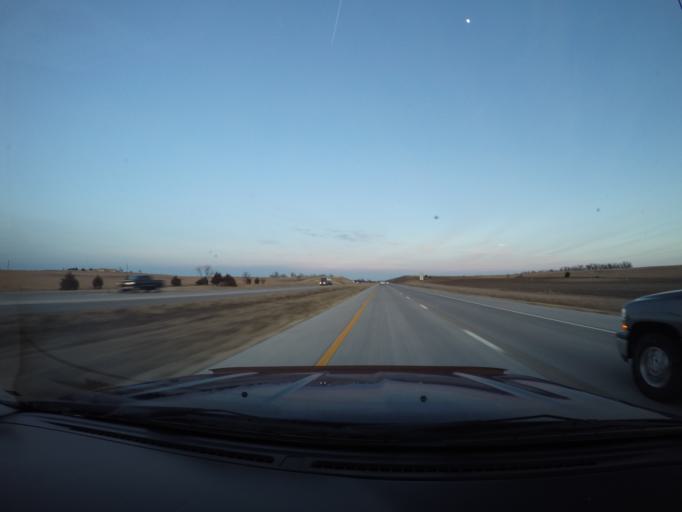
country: US
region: Kansas
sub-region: Dickinson County
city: Abilene
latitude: 38.9438
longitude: -97.1571
